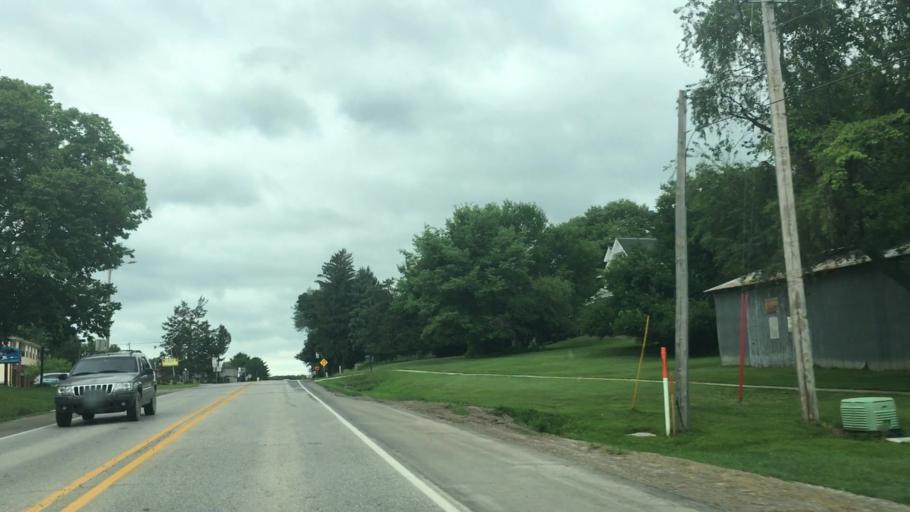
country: US
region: Iowa
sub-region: Johnson County
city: Tiffin
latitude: 41.7070
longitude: -91.6625
